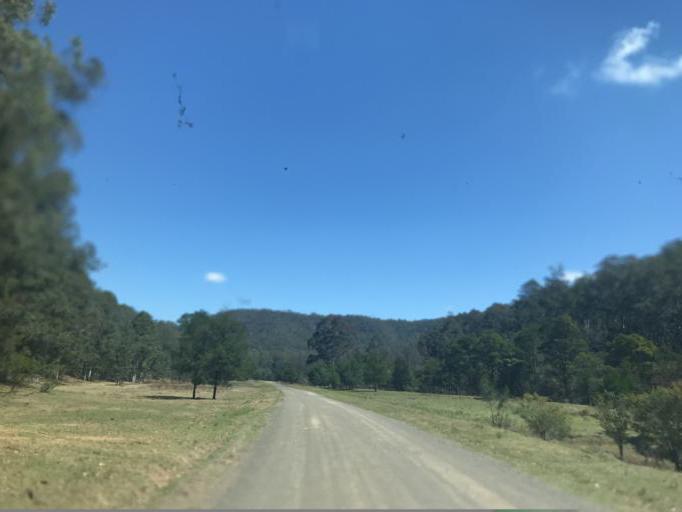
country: AU
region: New South Wales
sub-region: Wyong Shire
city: Little Jilliby
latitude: -33.2030
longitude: 150.9868
